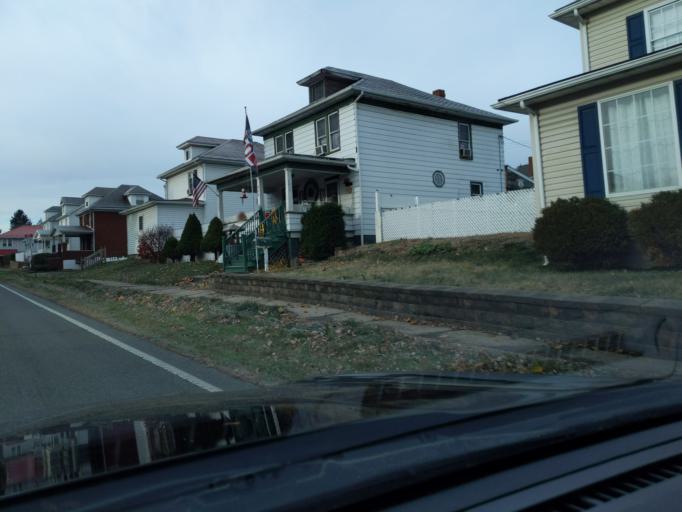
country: US
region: Pennsylvania
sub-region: Blair County
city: Greenwood
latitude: 40.5249
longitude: -78.3744
